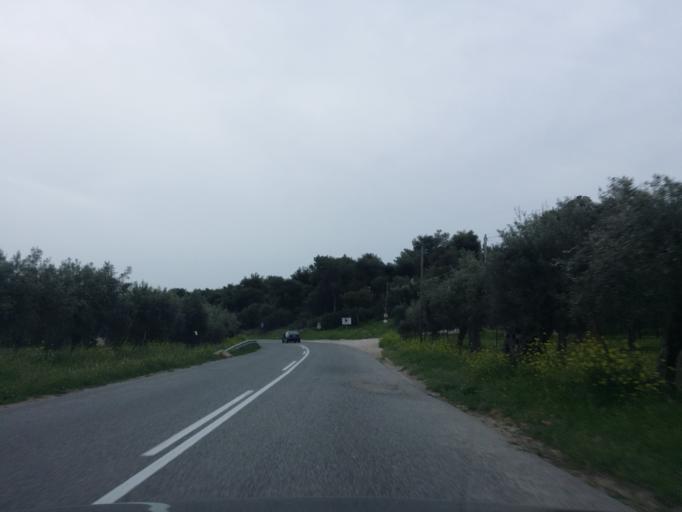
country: GR
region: Attica
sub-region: Nomarchia Dytikis Attikis
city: Mandra
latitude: 38.0860
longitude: 23.4840
